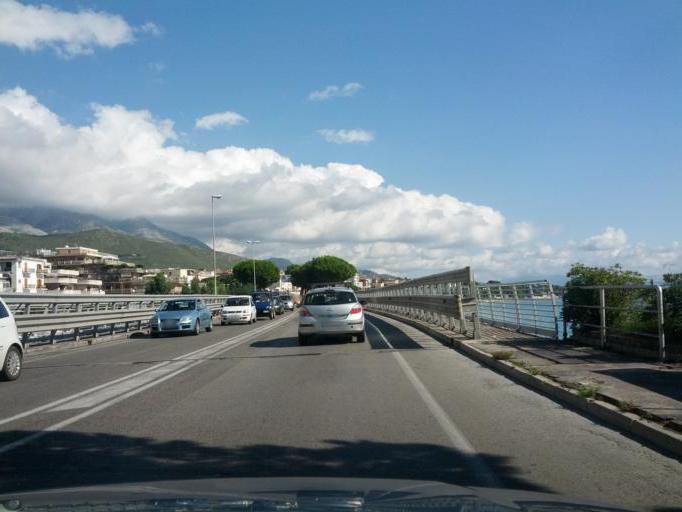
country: IT
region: Latium
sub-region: Provincia di Latina
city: Formia
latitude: 41.2583
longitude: 13.6141
